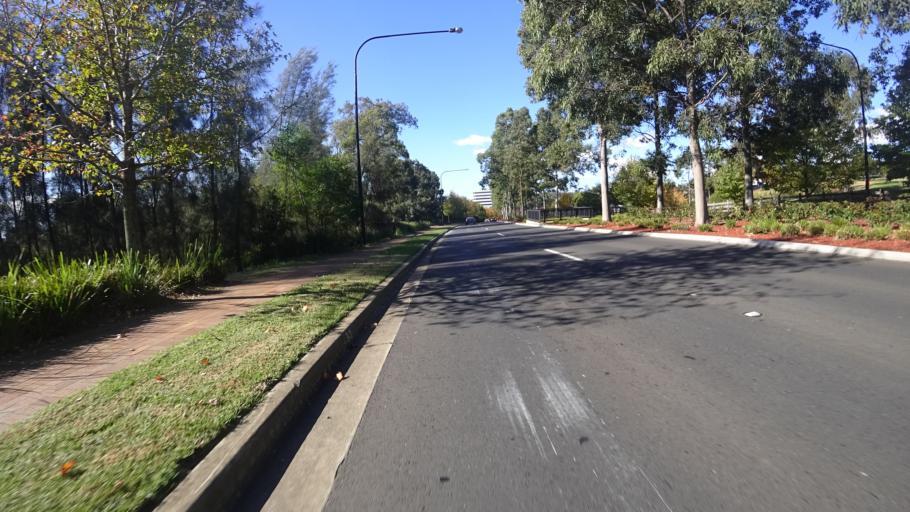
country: AU
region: New South Wales
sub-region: Blacktown
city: Stanhope Gardens
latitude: -33.7375
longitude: 150.9525
